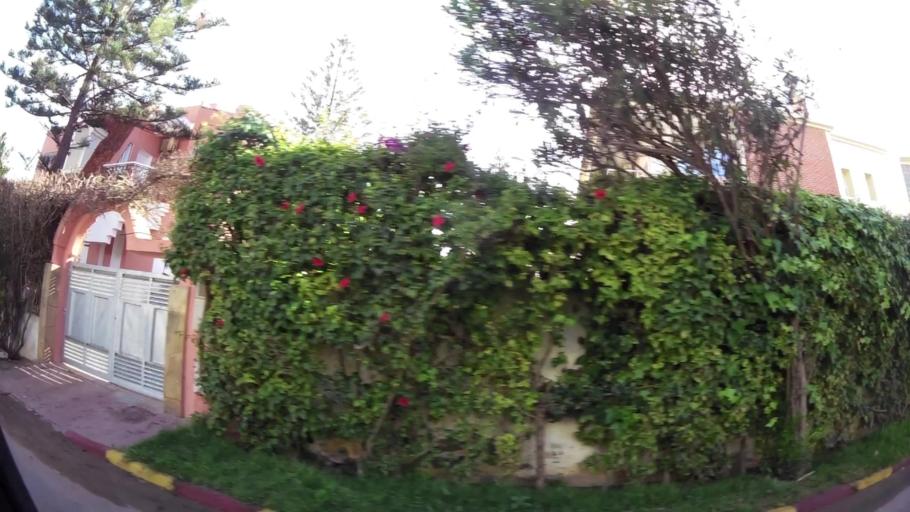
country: MA
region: Grand Casablanca
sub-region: Mohammedia
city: Mohammedia
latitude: 33.7117
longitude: -7.3560
